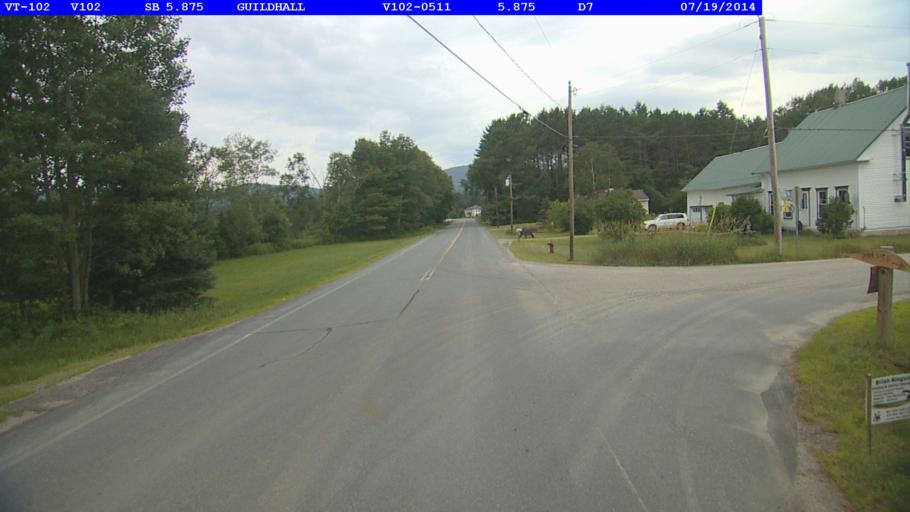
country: US
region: Vermont
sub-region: Essex County
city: Guildhall
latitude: 44.5663
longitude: -71.5879
